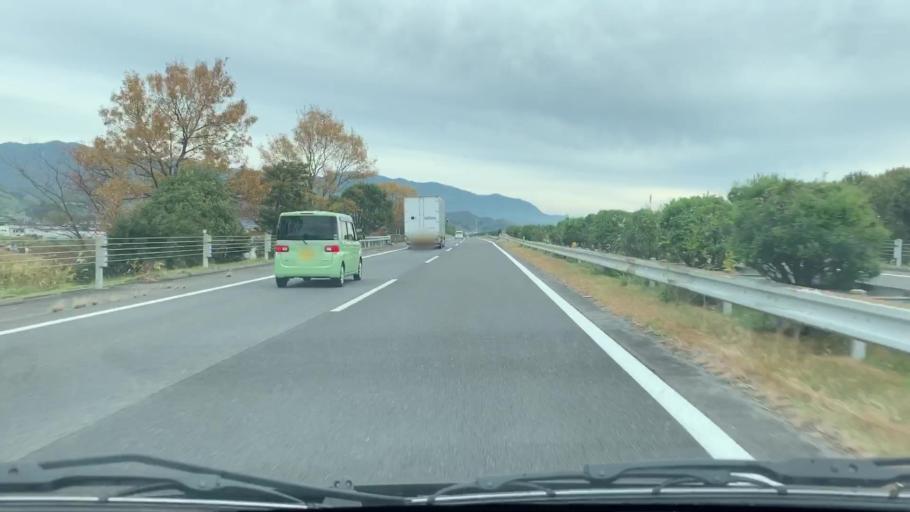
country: JP
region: Saga Prefecture
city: Saga-shi
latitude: 33.3111
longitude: 130.2494
